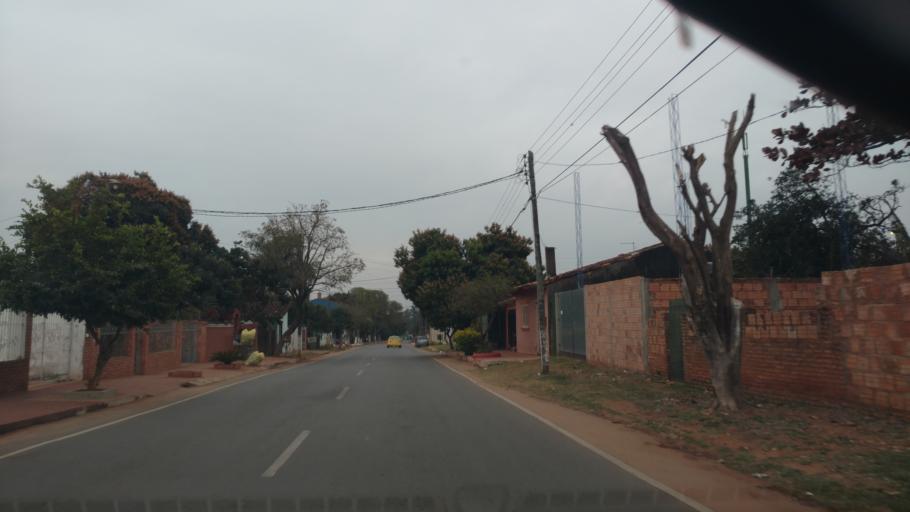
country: PY
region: Central
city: San Lorenzo
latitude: -25.3510
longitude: -57.4803
